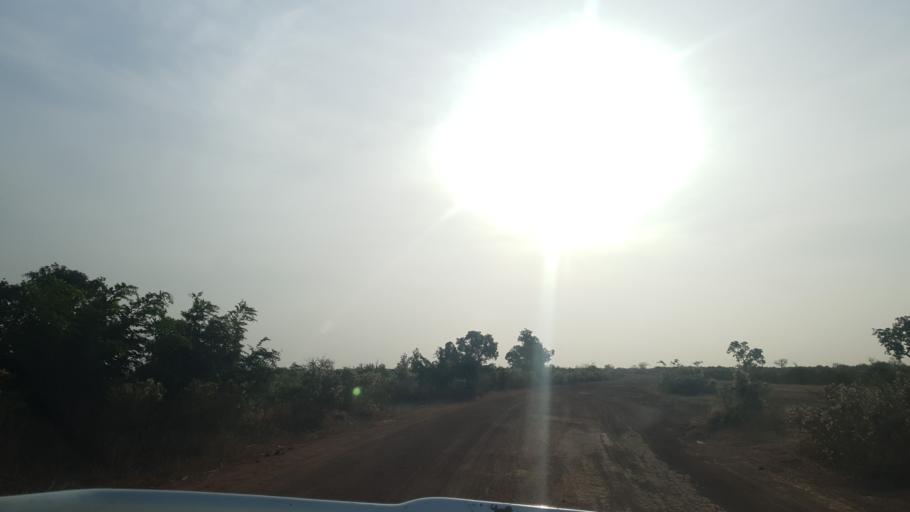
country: ML
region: Koulikoro
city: Dioila
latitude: 12.7693
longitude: -6.9252
